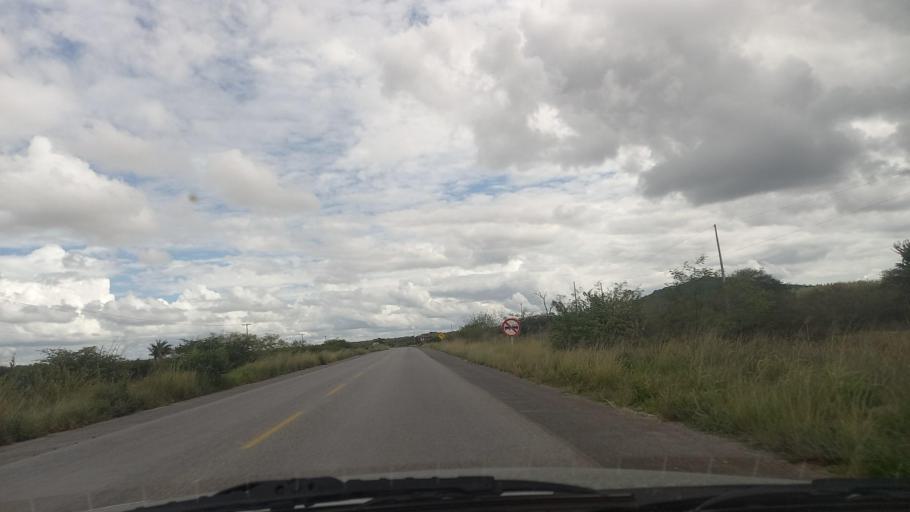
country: BR
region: Pernambuco
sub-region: Cachoeirinha
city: Cachoeirinha
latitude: -8.3484
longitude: -36.1679
